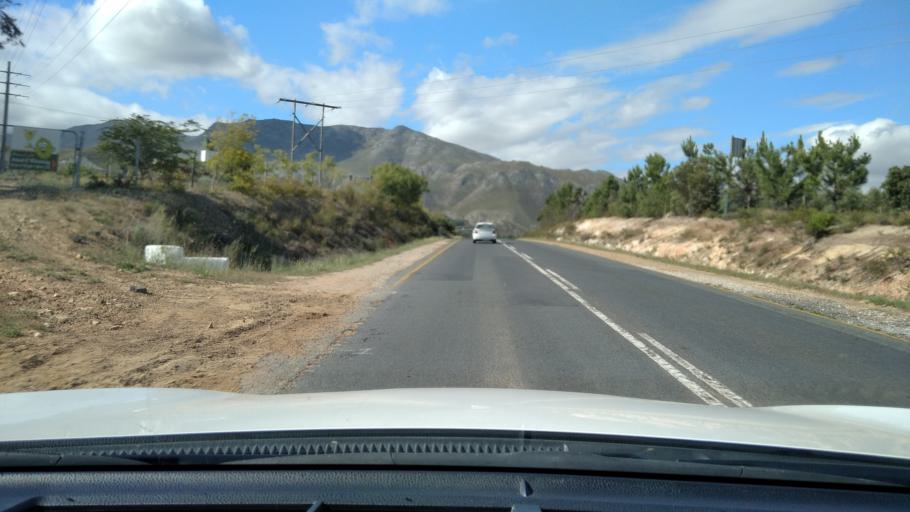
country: ZA
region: Western Cape
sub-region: Overberg District Municipality
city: Hermanus
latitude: -34.2352
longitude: 19.1860
